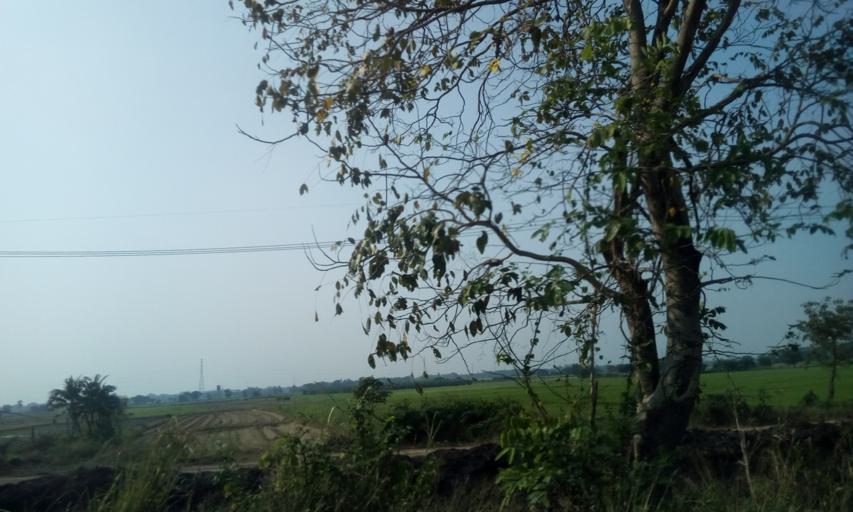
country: TH
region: Sing Buri
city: Tha Chang
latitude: 14.7355
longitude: 100.4347
